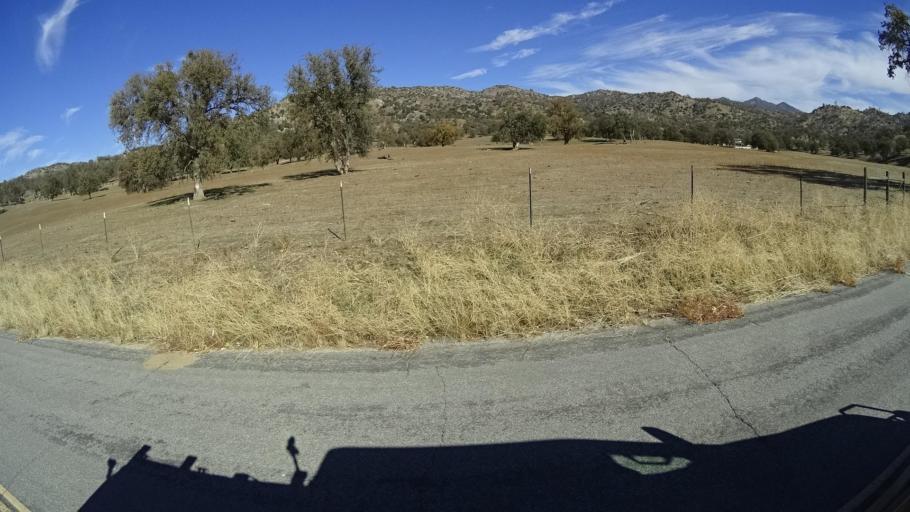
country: US
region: California
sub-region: Kern County
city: Alta Sierra
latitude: 35.6189
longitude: -118.7348
